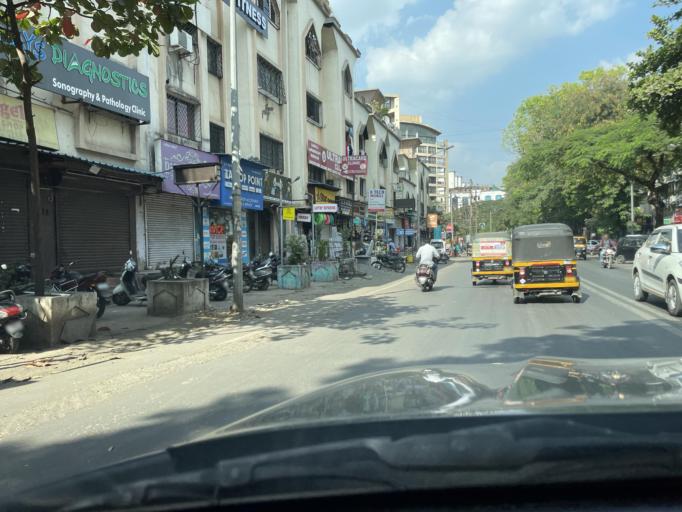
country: IN
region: Maharashtra
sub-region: Pune Division
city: Pune
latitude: 18.5012
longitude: 73.9005
